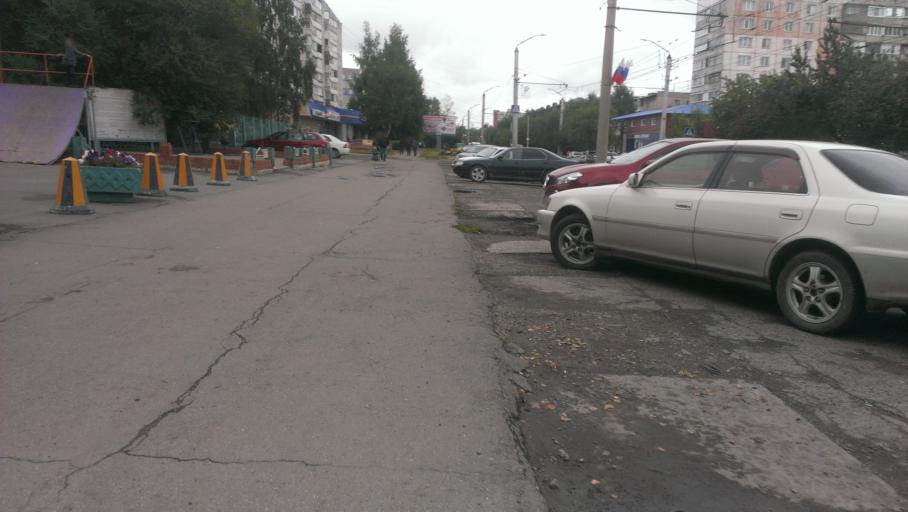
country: RU
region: Altai Krai
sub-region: Gorod Barnaulskiy
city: Barnaul
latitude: 53.3706
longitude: 83.6852
